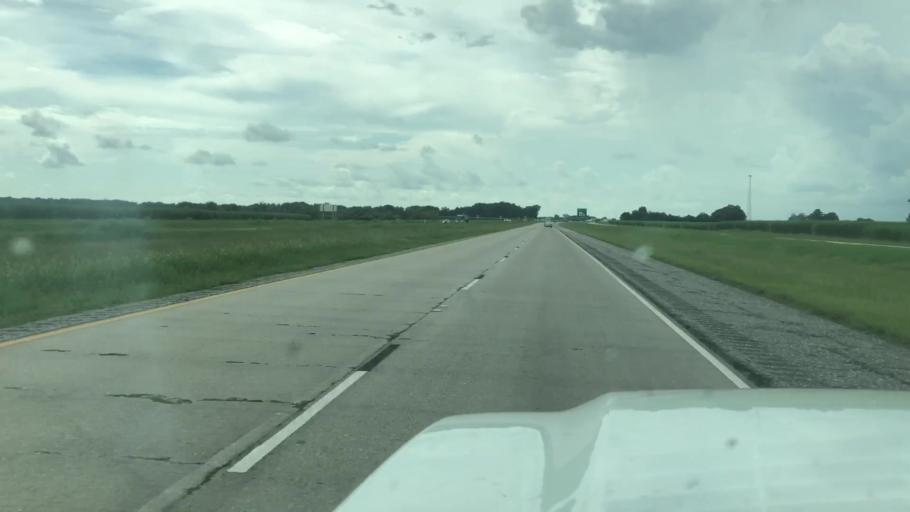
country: US
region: Louisiana
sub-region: Iberia Parish
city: Jeanerette
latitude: 29.8588
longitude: -91.6157
